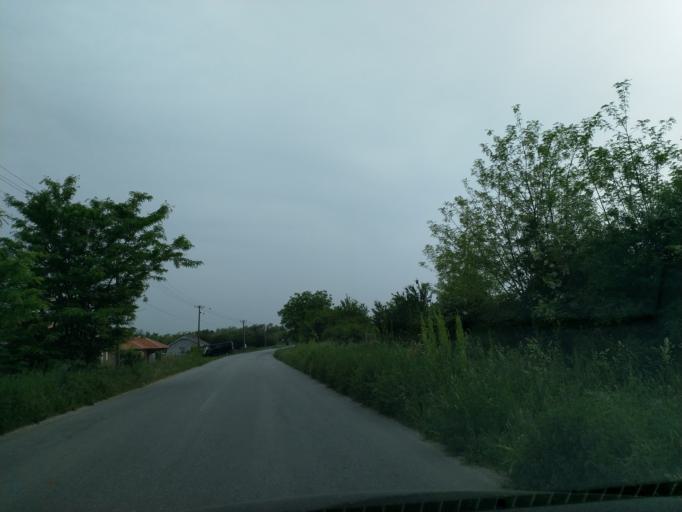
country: RS
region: Central Serbia
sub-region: Pomoravski Okrug
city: Jagodina
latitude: 43.9699
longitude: 21.2355
